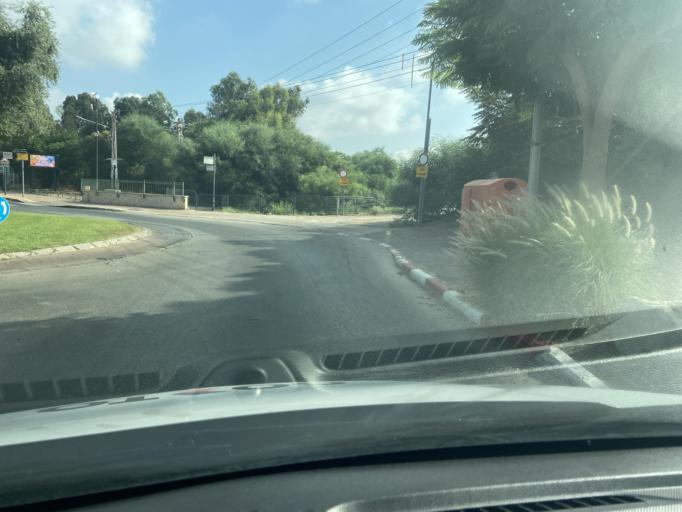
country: IL
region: Central District
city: Yehud
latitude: 32.0402
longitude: 34.8832
